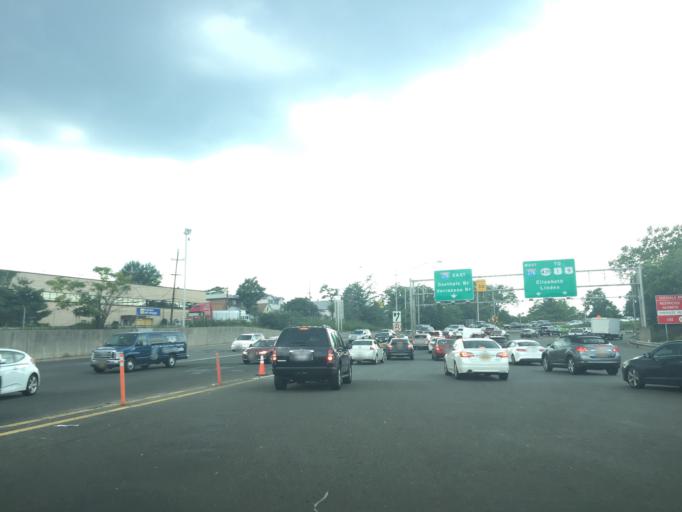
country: US
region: New Jersey
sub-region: Union County
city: Elizabeth
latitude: 40.6413
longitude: -74.2110
